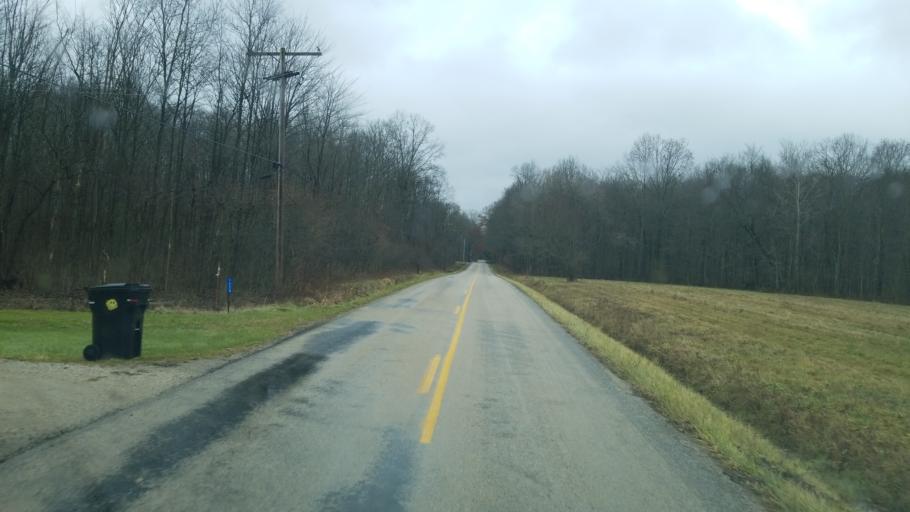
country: US
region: Ohio
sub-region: Ashtabula County
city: Roaming Shores
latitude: 41.7188
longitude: -80.8747
